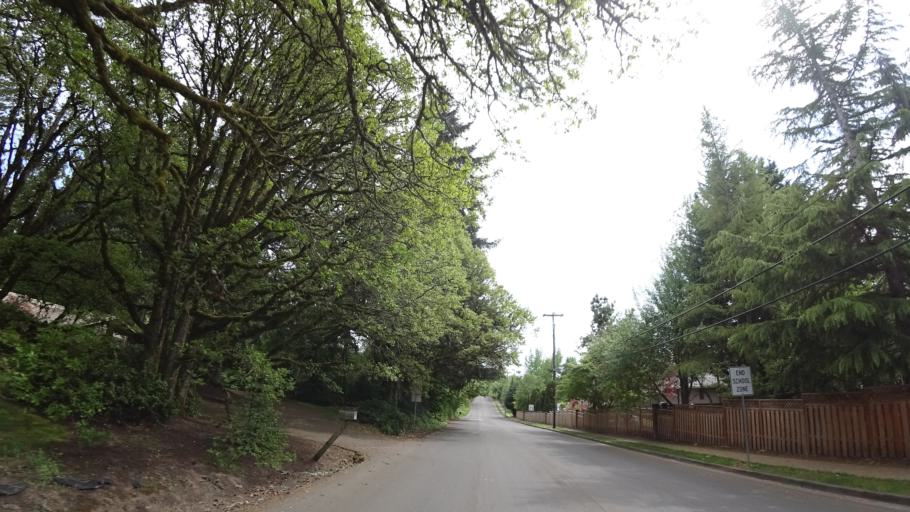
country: US
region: Oregon
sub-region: Washington County
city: Aloha
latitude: 45.5103
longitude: -122.9226
